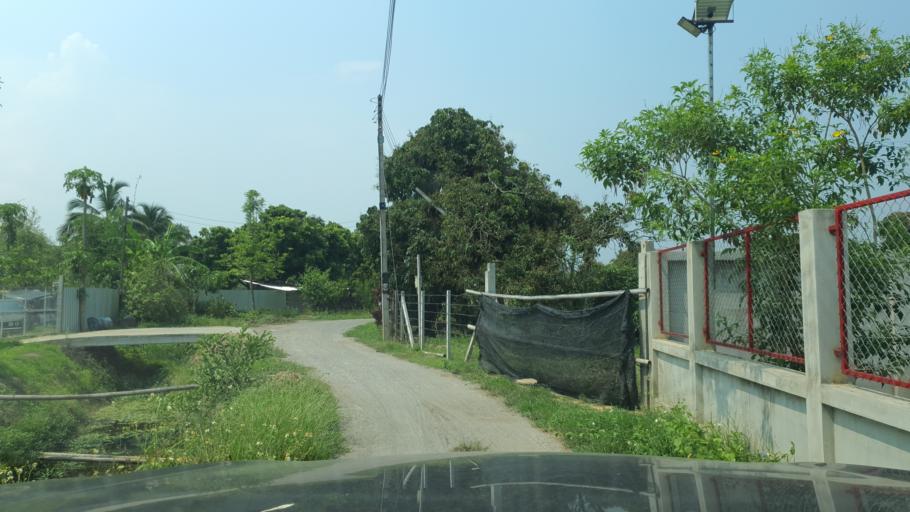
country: TH
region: Chiang Mai
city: Saraphi
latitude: 18.6739
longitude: 98.9880
